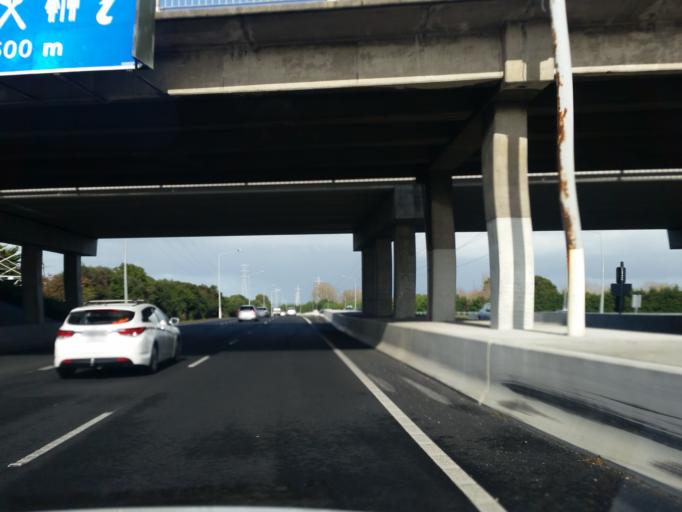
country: NZ
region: Auckland
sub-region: Auckland
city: Papakura
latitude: -37.0733
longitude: 174.9289
